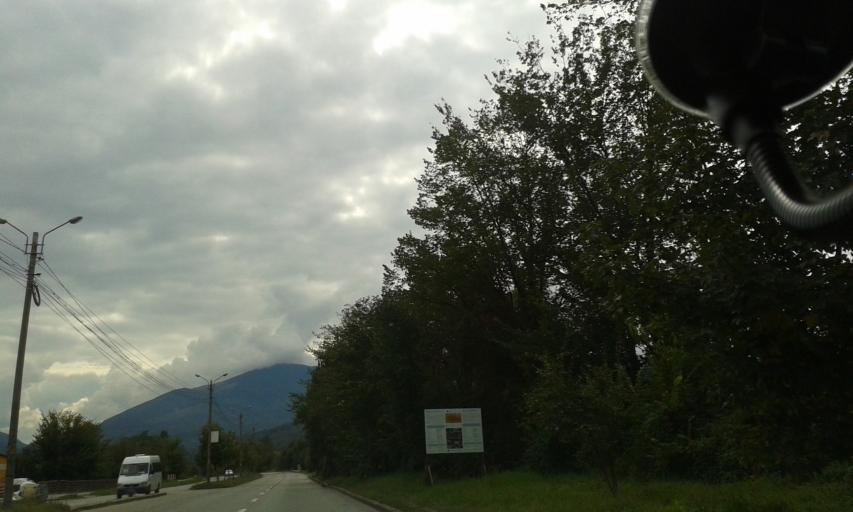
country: RO
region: Hunedoara
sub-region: Municipiul Petrosani
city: Petrosani
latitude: 45.4184
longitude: 23.3676
